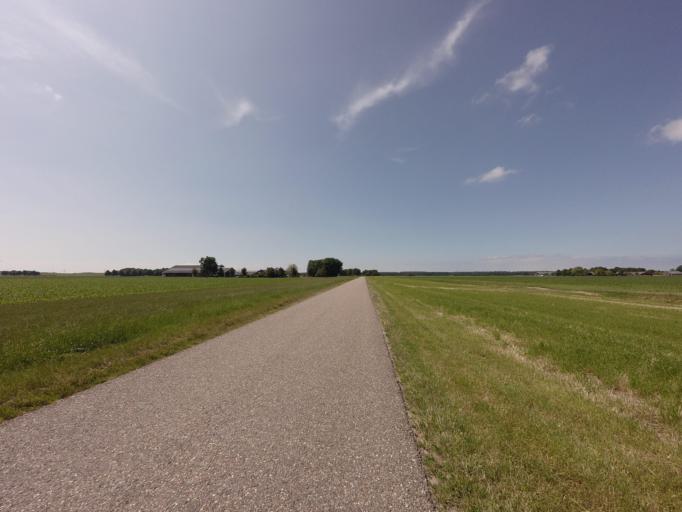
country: NL
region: Flevoland
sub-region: Gemeente Lelystad
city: Lelystad
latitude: 52.4381
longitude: 5.4644
